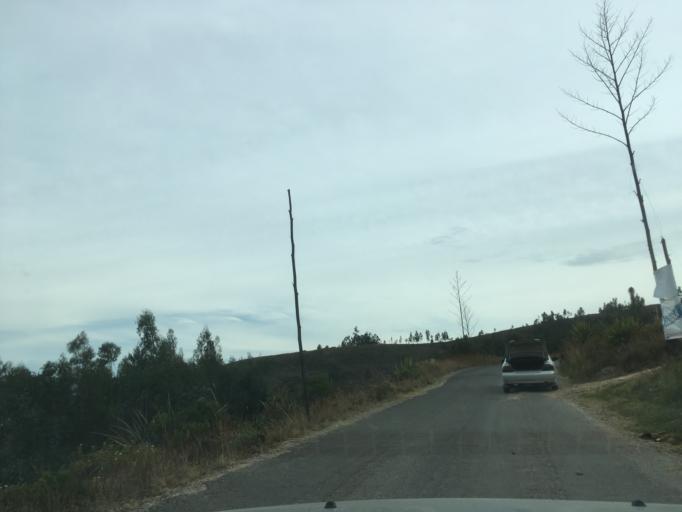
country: CO
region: Boyaca
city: Firavitoba
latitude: 5.6752
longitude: -73.0120
